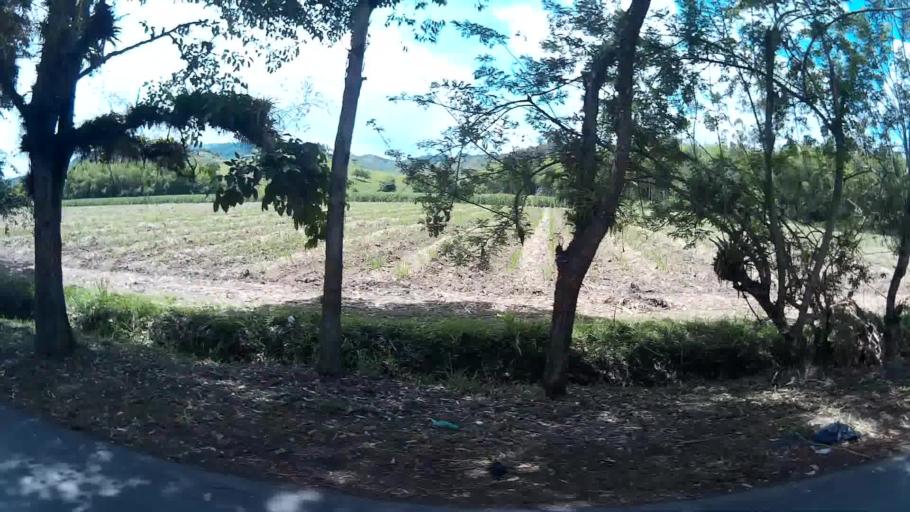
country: CO
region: Risaralda
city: La Virginia
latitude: 4.9038
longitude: -75.8693
